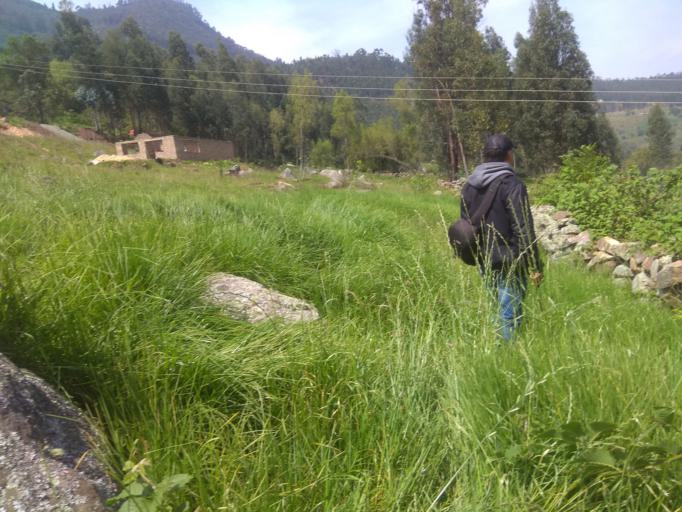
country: CO
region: Boyaca
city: Socha Viejo
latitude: 5.9808
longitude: -72.7211
